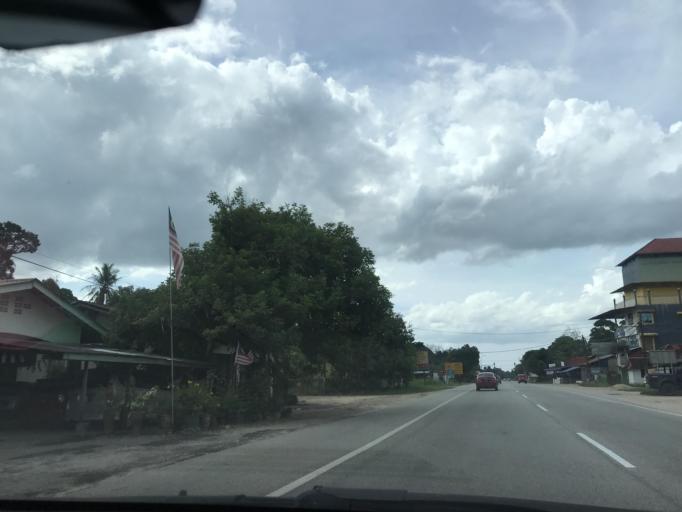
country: MY
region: Kelantan
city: Kampong Pangkal Kalong
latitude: 5.9240
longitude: 102.1897
